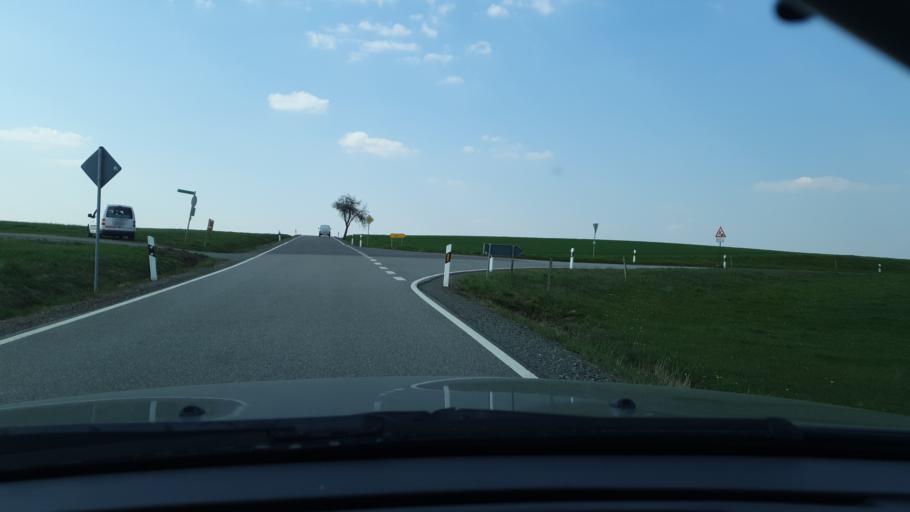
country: DE
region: Rheinland-Pfalz
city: Knopp-Labach
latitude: 49.3380
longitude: 7.4934
